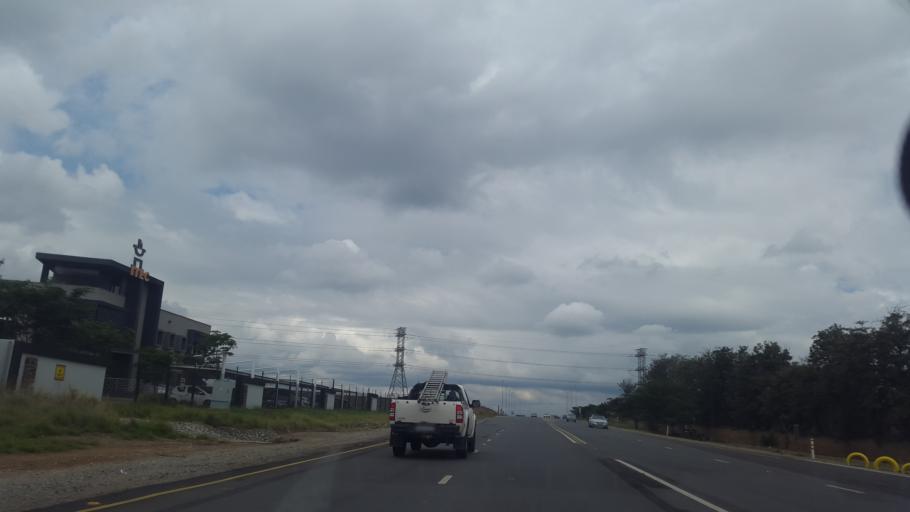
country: ZA
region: Gauteng
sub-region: City of Johannesburg Metropolitan Municipality
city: Diepsloot
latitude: -25.9834
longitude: 27.9786
